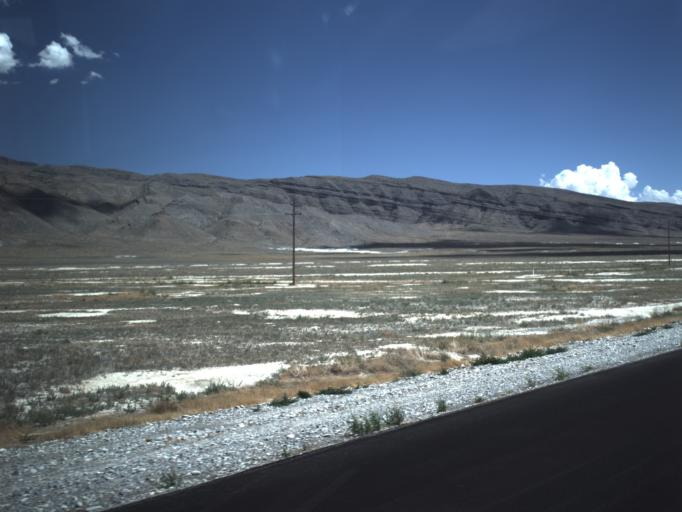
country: US
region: Utah
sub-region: Beaver County
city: Milford
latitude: 39.0665
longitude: -113.4515
